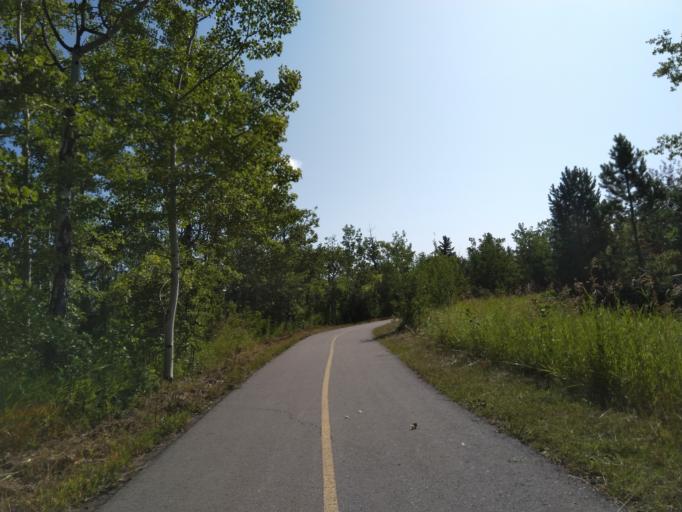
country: CA
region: Alberta
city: Calgary
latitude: 51.0968
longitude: -114.2467
